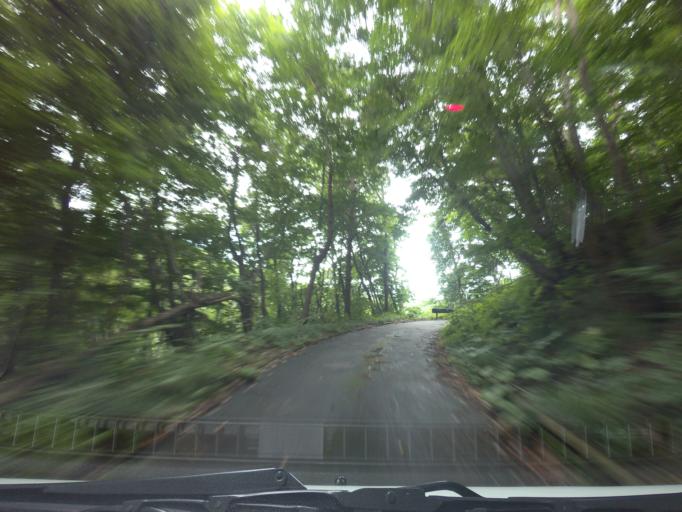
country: JP
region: Fukushima
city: Motomiya
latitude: 37.5597
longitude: 140.3025
